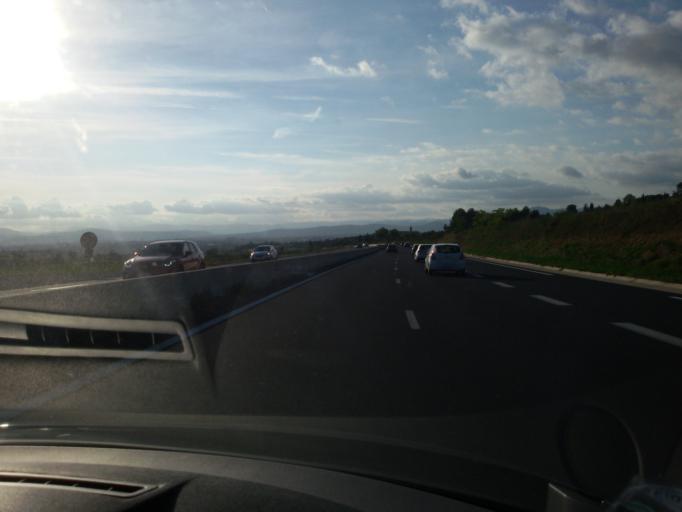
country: FR
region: Languedoc-Roussillon
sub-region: Departement de l'Herault
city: Gignac
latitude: 43.6423
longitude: 3.5680
